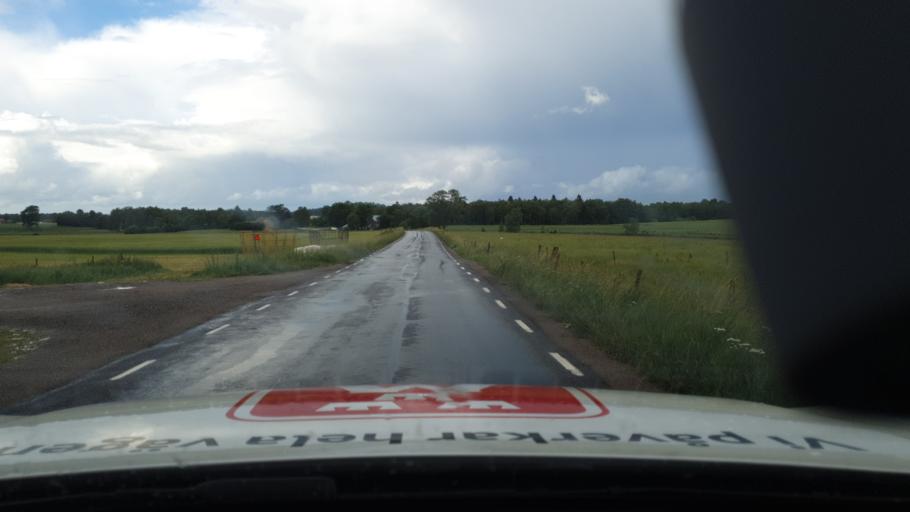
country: SE
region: Vaestra Goetaland
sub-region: Falkopings Kommun
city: Falkoeping
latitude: 58.0713
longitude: 13.6352
